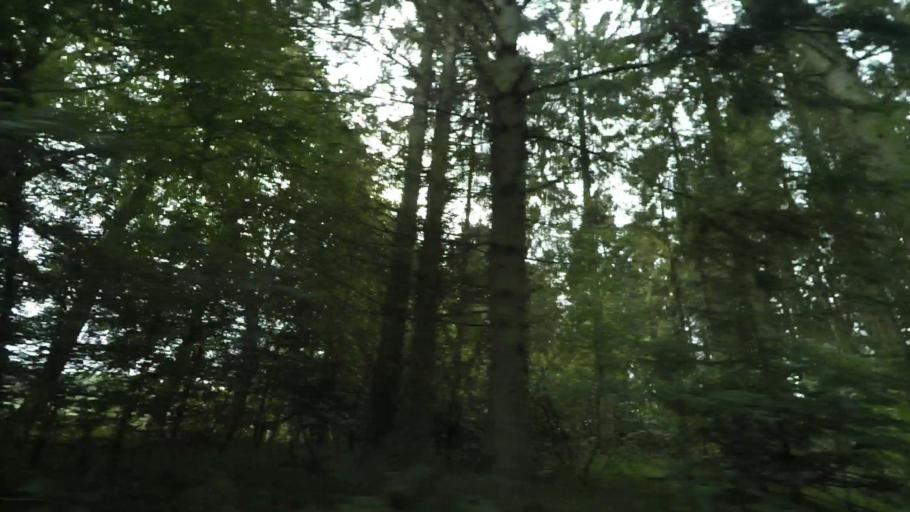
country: DK
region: Central Jutland
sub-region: Syddjurs Kommune
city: Ryomgard
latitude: 56.3455
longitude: 10.4904
